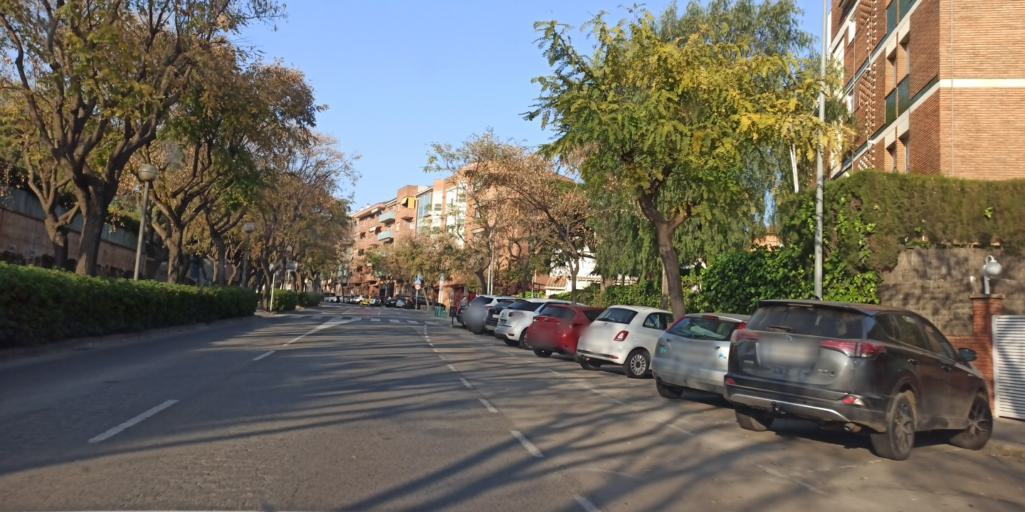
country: ES
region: Catalonia
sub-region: Provincia de Barcelona
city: Sant Just Desvern
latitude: 41.3836
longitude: 2.0713
